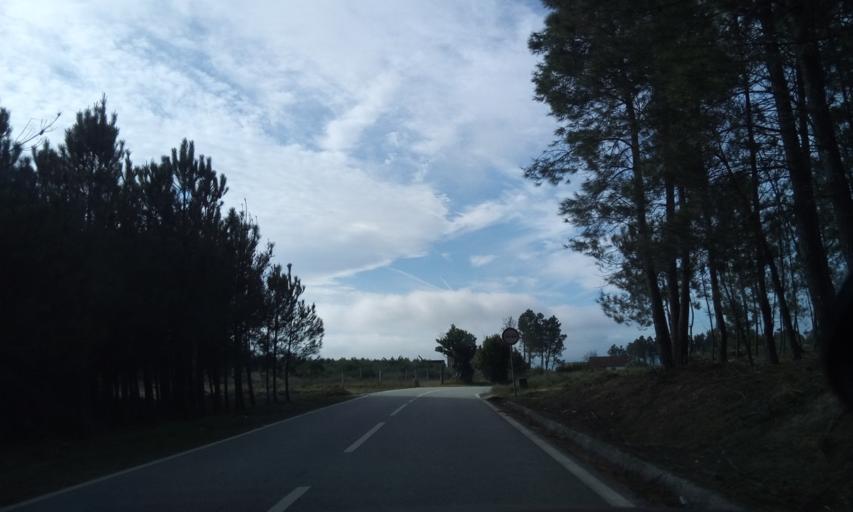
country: PT
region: Guarda
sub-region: Aguiar da Beira
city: Aguiar da Beira
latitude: 40.7557
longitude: -7.5429
